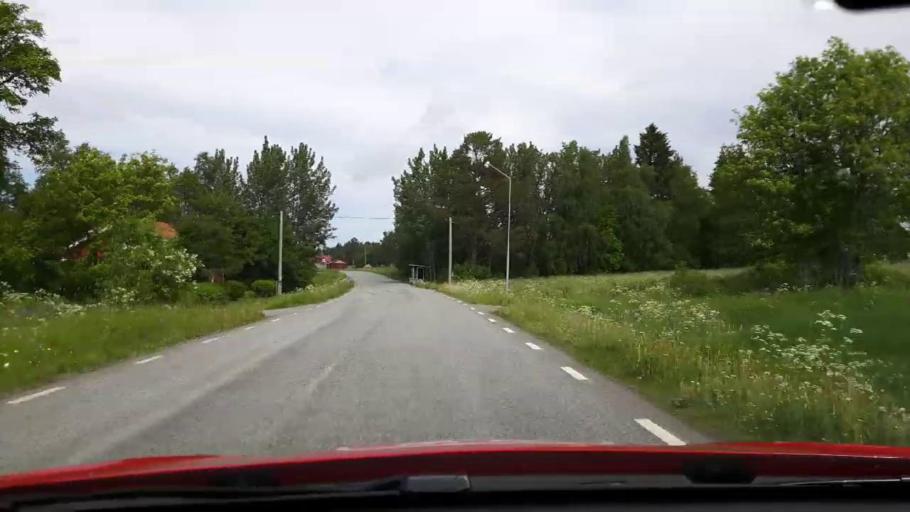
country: SE
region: Jaemtland
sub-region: OEstersunds Kommun
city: Ostersund
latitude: 63.0441
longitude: 14.4561
